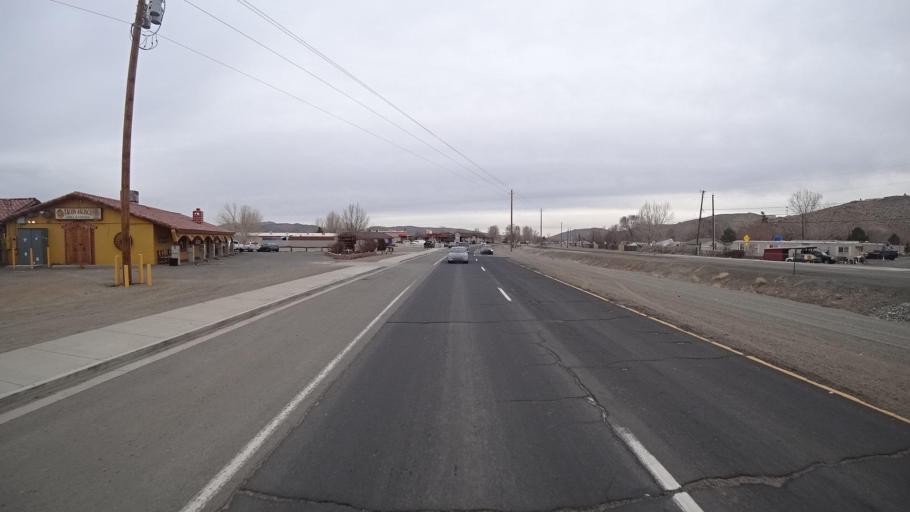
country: US
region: Nevada
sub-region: Washoe County
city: Lemmon Valley
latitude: 39.6368
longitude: -119.8437
